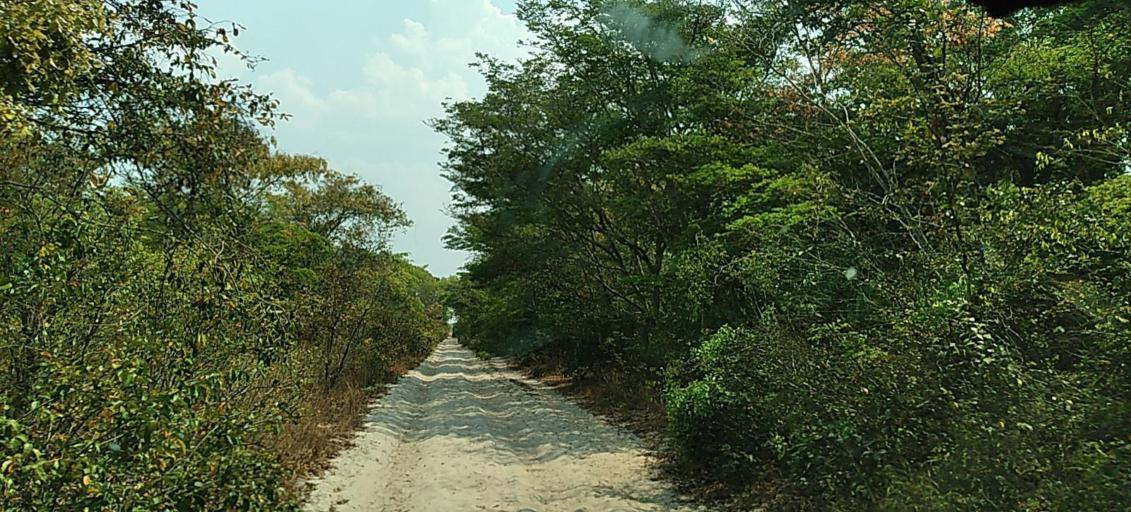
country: ZM
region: North-Western
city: Kabompo
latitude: -13.3887
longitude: 23.7640
